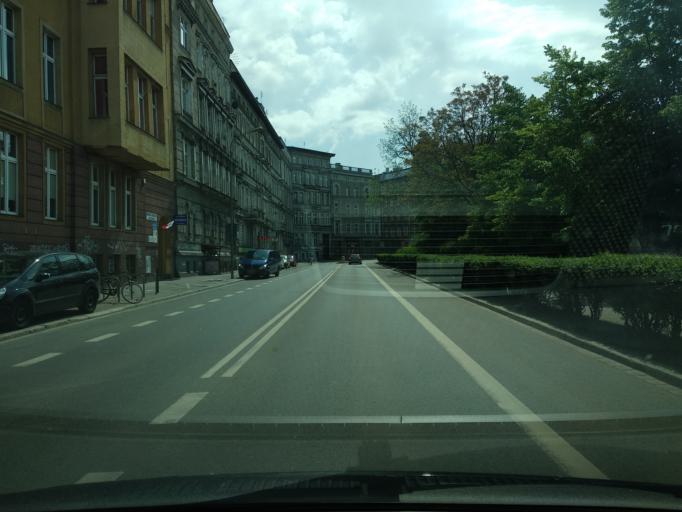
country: PL
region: Lower Silesian Voivodeship
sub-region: Powiat wroclawski
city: Wroclaw
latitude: 51.1203
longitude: 17.0366
